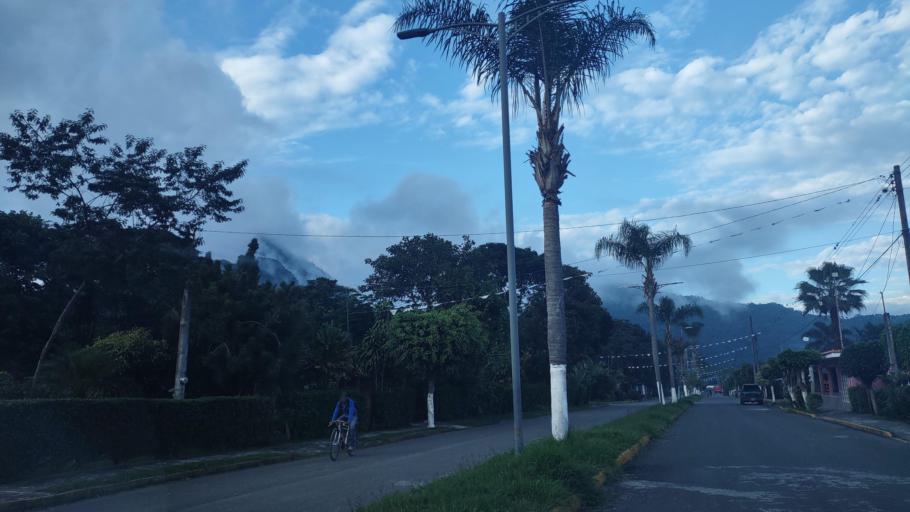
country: MX
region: Veracruz
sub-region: Ixtaczoquitlan
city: Buenavista
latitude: 18.9188
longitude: -97.0445
